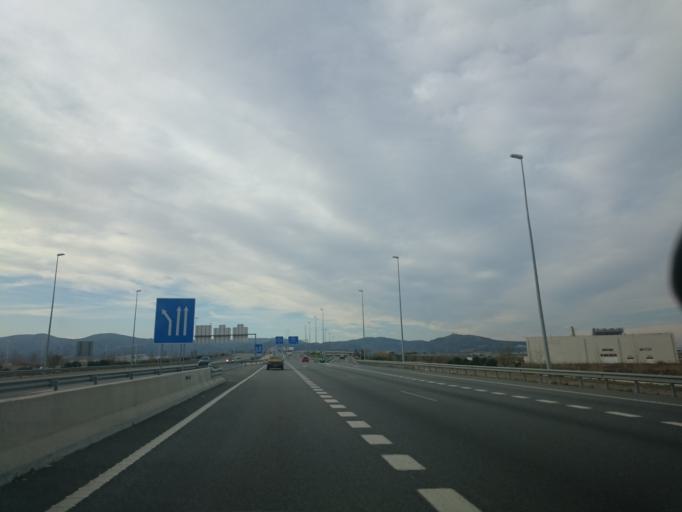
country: ES
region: Catalonia
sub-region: Provincia de Barcelona
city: Viladecans
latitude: 41.2933
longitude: 2.0556
